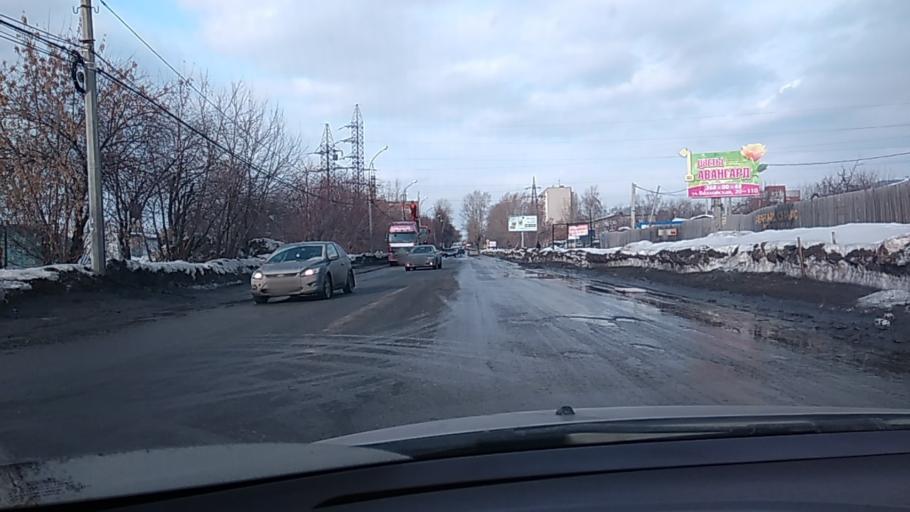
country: RU
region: Sverdlovsk
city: Yekaterinburg
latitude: 56.8662
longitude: 60.6528
